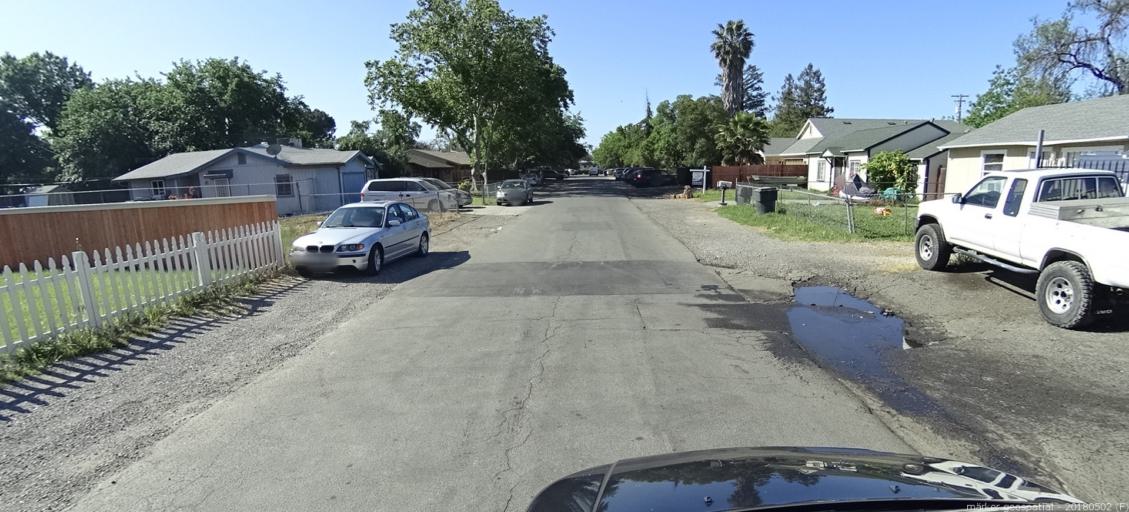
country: US
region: California
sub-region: Sacramento County
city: Arden-Arcade
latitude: 38.6106
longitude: -121.4315
